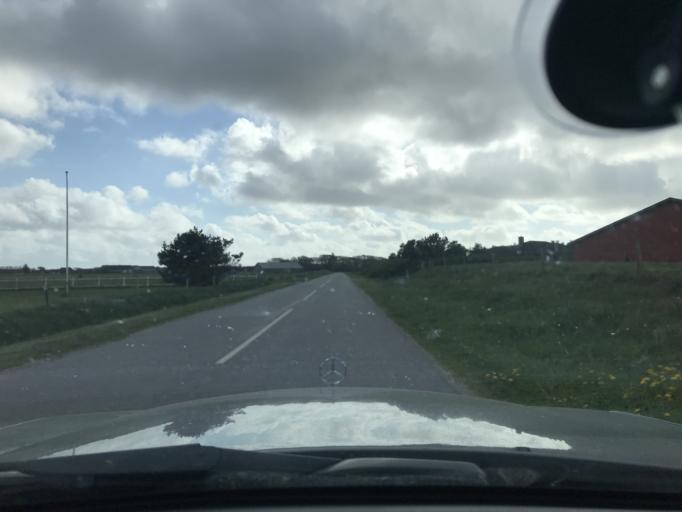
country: DE
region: Schleswig-Holstein
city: List
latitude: 55.1809
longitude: 8.5604
